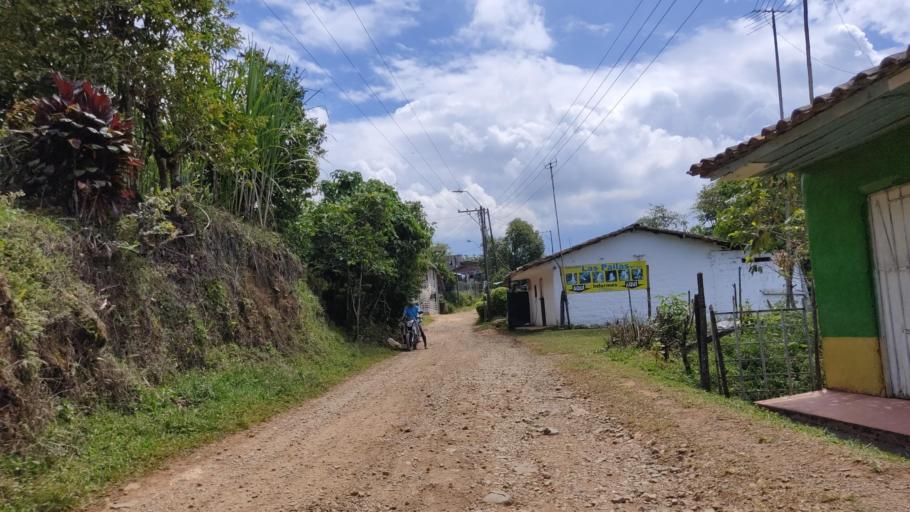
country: CO
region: Valle del Cauca
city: Jamundi
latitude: 3.2127
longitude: -76.6562
